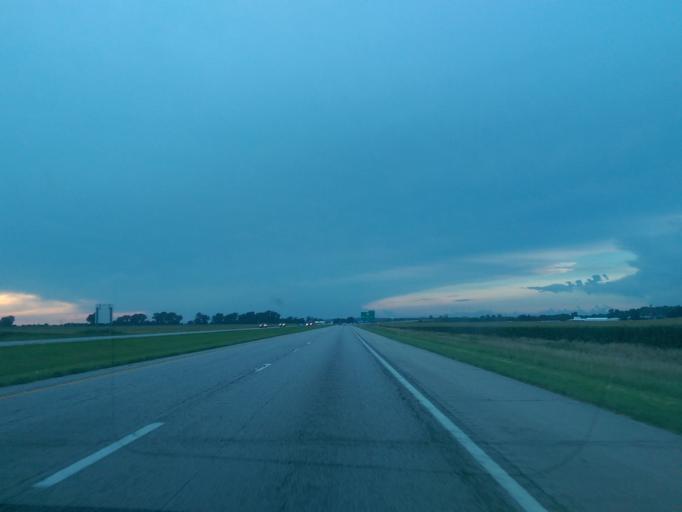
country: US
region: Missouri
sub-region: Holt County
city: Mound City
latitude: 40.1166
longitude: -95.2261
